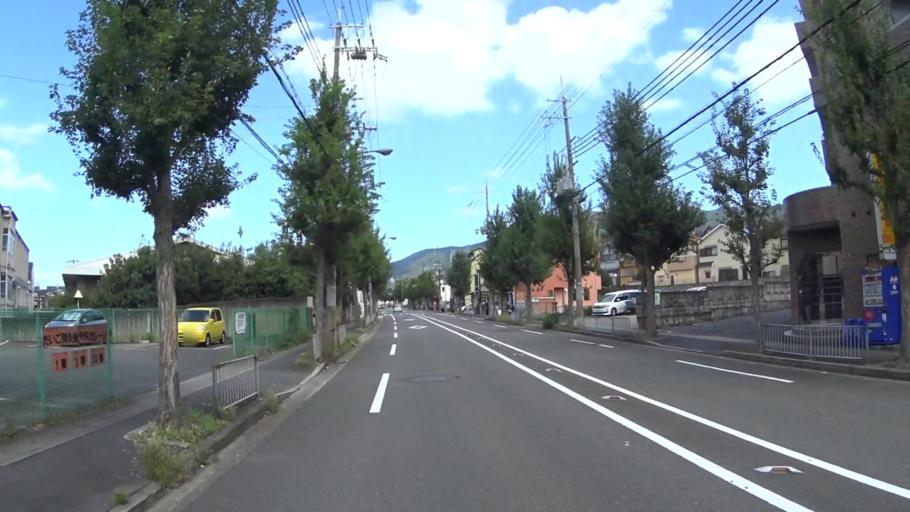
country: JP
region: Kyoto
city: Uji
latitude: 34.9442
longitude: 135.8130
